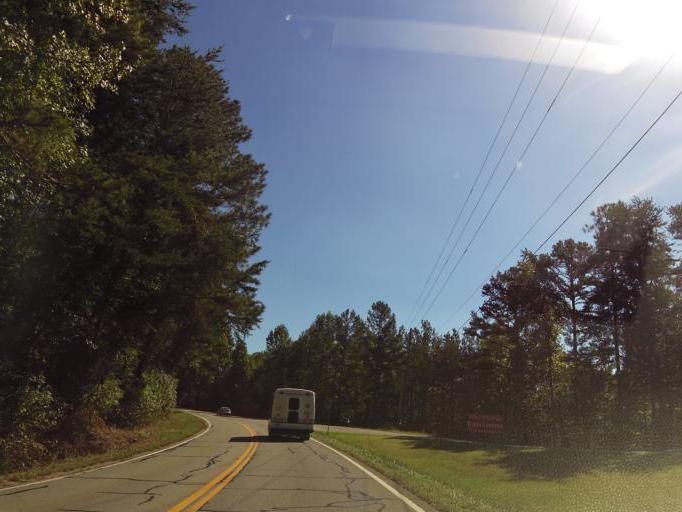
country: US
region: Georgia
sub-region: Pickens County
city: Nelson
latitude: 34.4127
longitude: -84.2945
